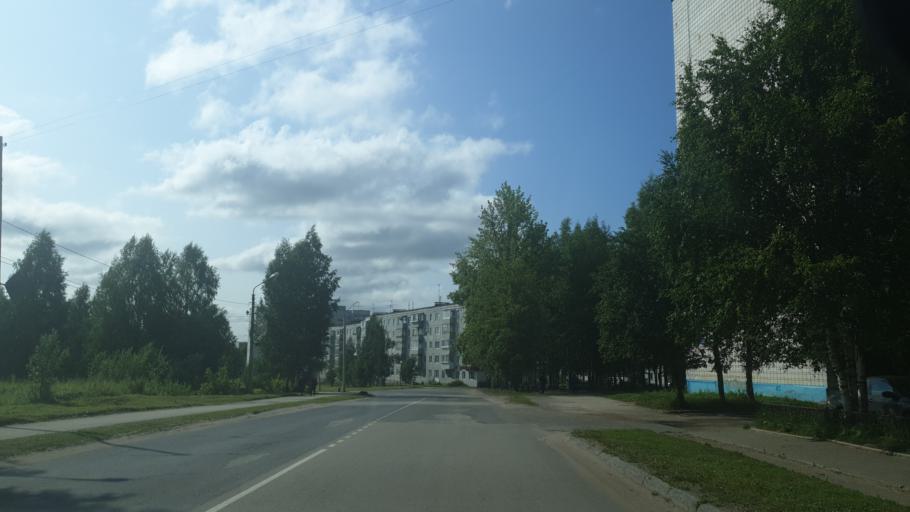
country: RU
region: Komi Republic
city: Ezhva
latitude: 61.7914
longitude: 50.7499
